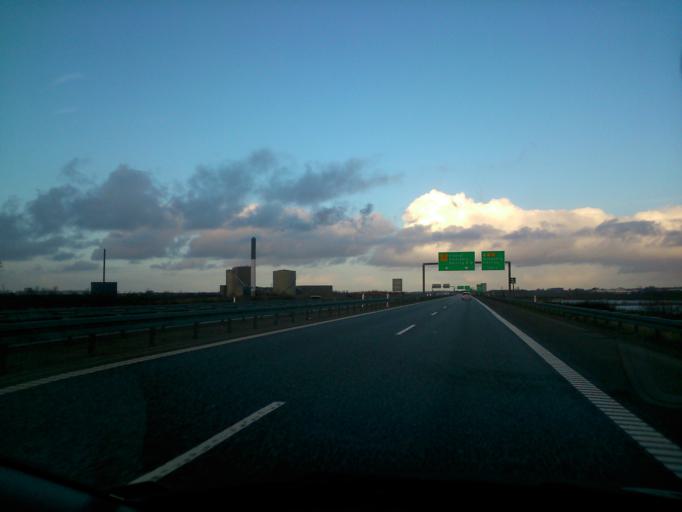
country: DK
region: Central Jutland
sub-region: Herning Kommune
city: Lind
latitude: 56.1141
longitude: 9.0108
